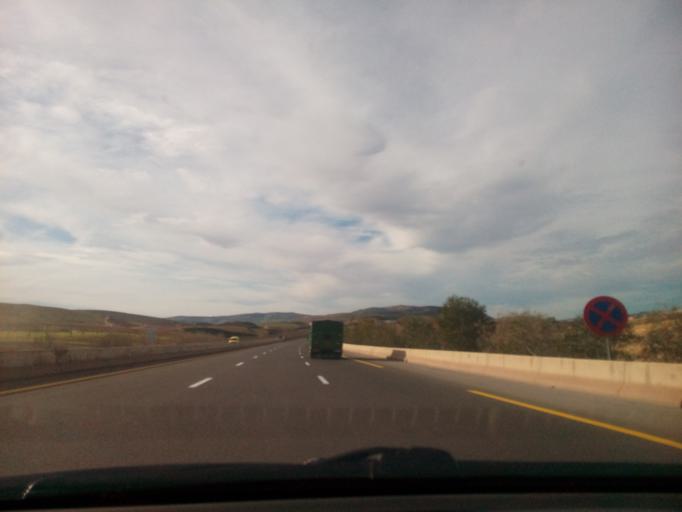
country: DZ
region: Sidi Bel Abbes
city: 'Ain el Berd
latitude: 35.4573
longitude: -0.3877
